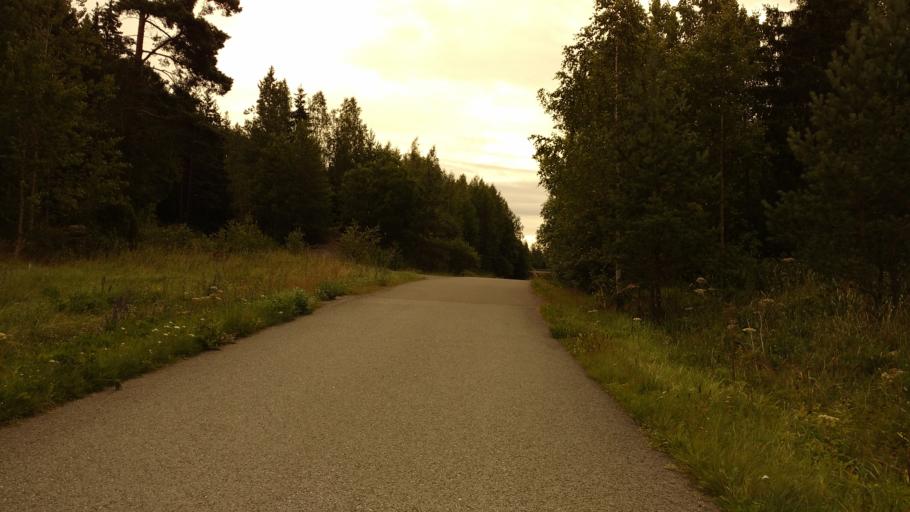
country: FI
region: Varsinais-Suomi
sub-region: Turku
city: Piikkioe
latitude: 60.4352
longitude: 22.4525
